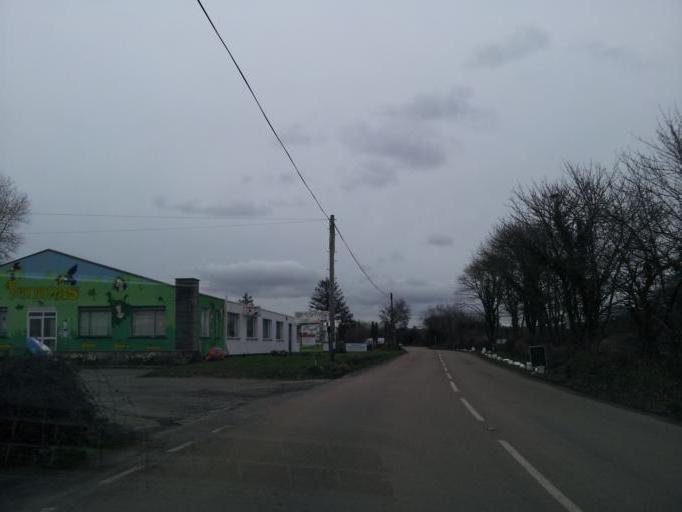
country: GB
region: England
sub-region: Cornwall
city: Redruth
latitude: 50.2593
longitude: -5.2570
